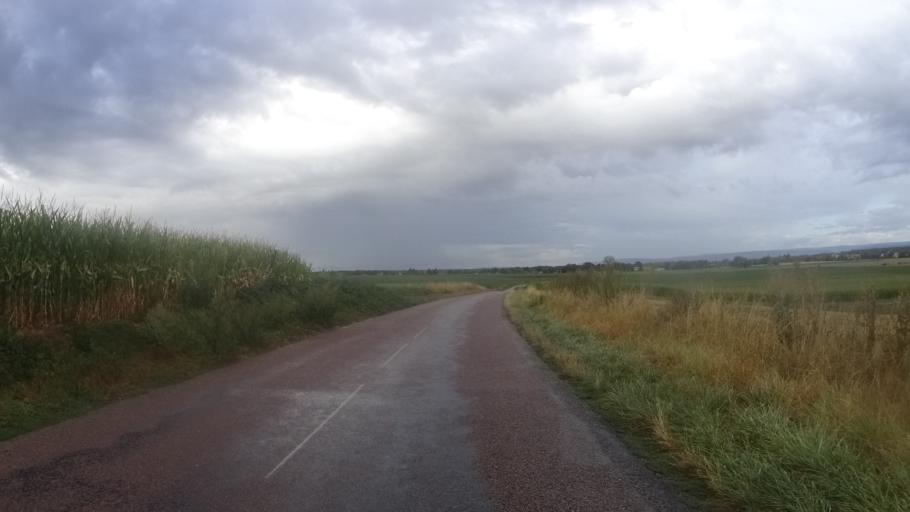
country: FR
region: Bourgogne
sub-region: Departement de Saone-et-Loire
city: Gergy
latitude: 46.9485
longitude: 4.9330
